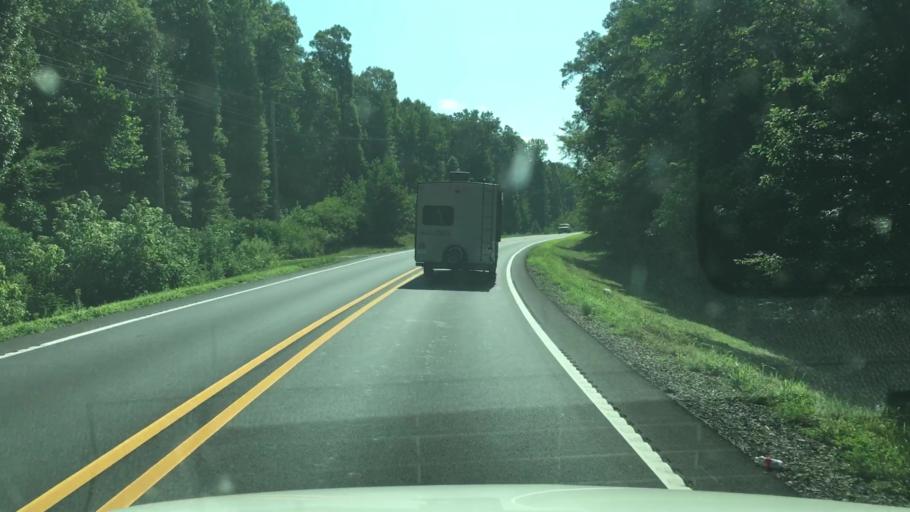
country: US
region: Arkansas
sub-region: Garland County
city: Rockwell
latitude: 34.5233
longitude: -93.3309
